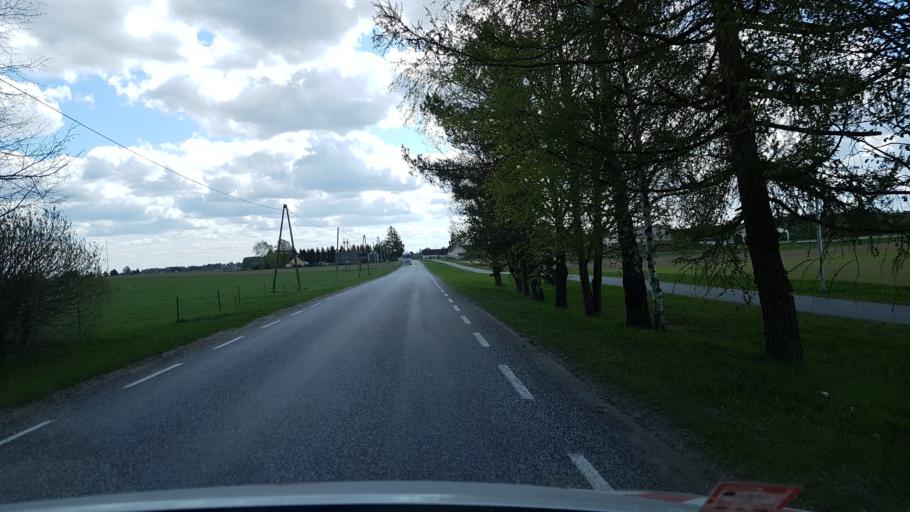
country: EE
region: Jogevamaa
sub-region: Poltsamaa linn
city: Poltsamaa
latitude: 58.6797
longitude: 25.9548
